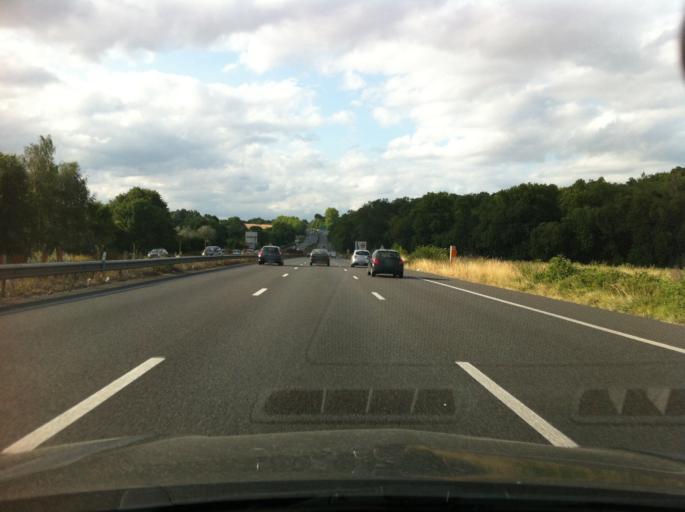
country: FR
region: Ile-de-France
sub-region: Departement de Seine-et-Marne
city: Brie-Comte-Robert
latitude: 48.6679
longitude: 2.6125
